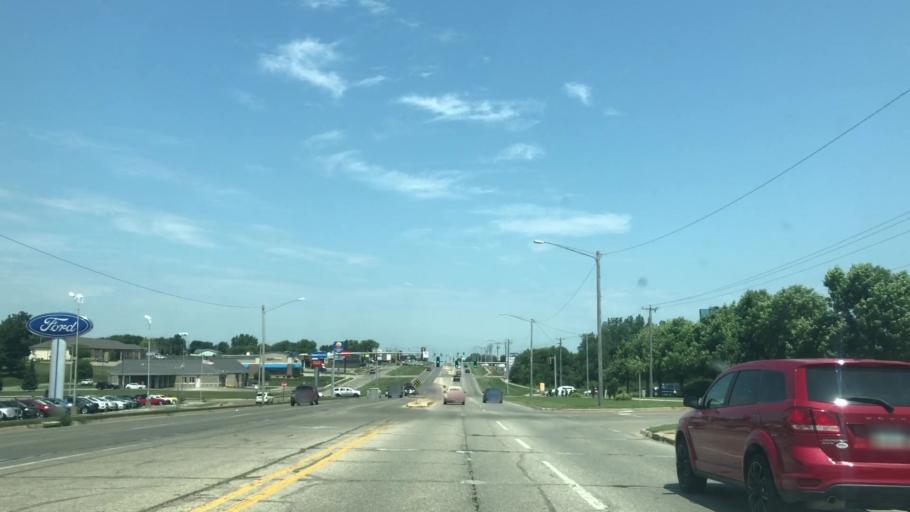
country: US
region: Iowa
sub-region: Marshall County
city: Marshalltown
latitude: 42.0116
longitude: -92.9123
